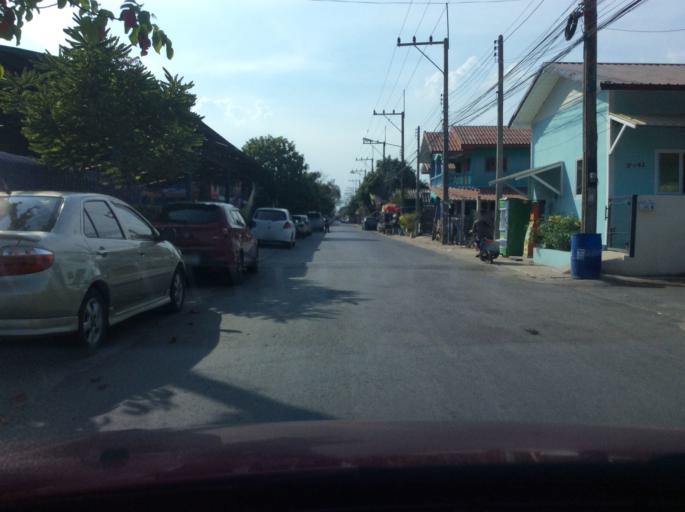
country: TH
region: Pathum Thani
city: Lam Luk Ka
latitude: 13.9673
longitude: 100.7434
